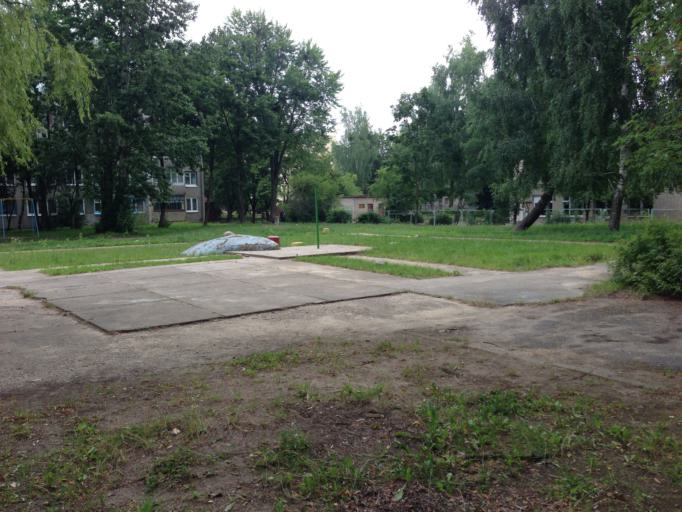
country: BY
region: Grodnenskaya
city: Hrodna
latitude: 53.7057
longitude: 23.8082
